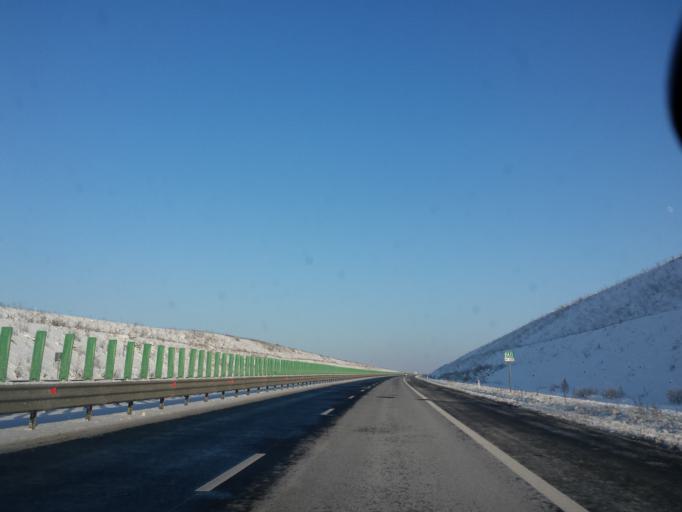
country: RO
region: Alba
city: Vurpar
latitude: 45.9567
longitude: 23.4389
